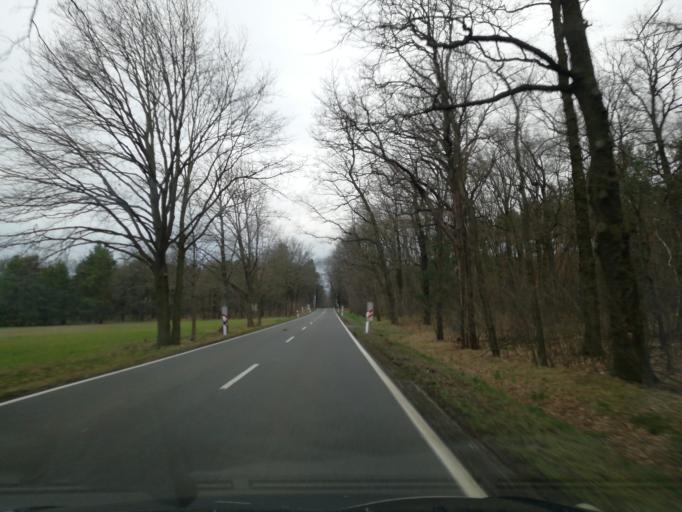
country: DE
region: Brandenburg
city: Vetschau
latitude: 51.7425
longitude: 14.0523
